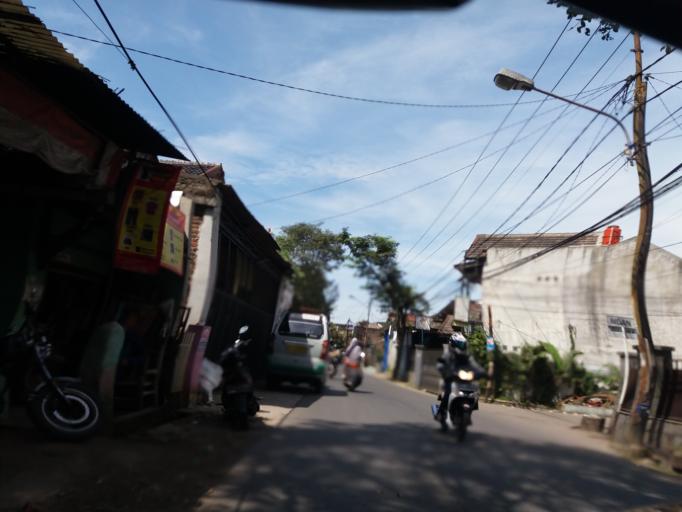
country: ID
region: West Java
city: Margahayukencana
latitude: -6.9505
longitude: 107.5735
